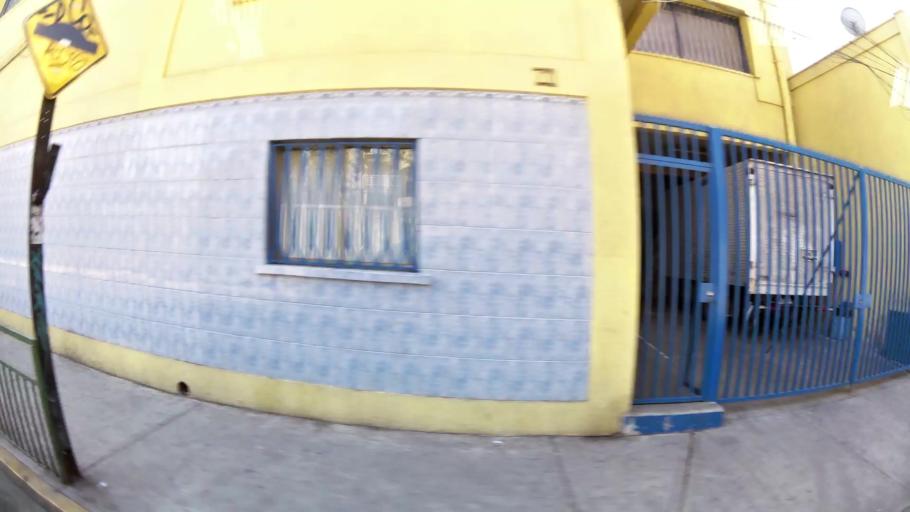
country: CL
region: Santiago Metropolitan
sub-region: Provincia de Santiago
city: Santiago
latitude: -33.4257
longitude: -70.6477
